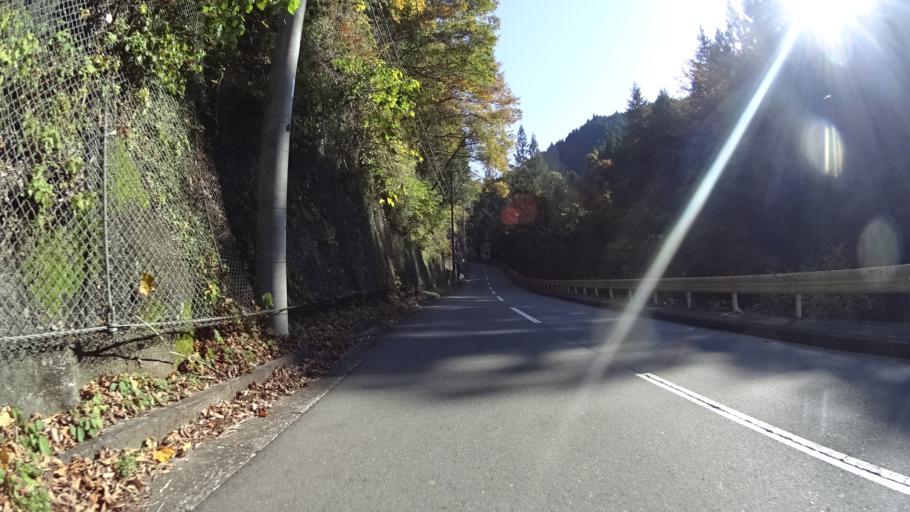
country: JP
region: Yamanashi
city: Uenohara
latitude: 35.7088
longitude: 139.0958
